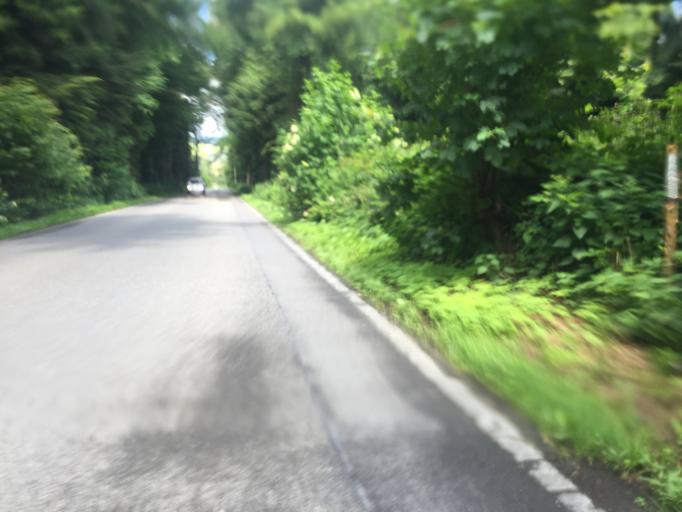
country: CH
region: Bern
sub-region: Bern-Mittelland District
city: Kirchlindach
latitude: 46.9882
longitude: 7.4124
